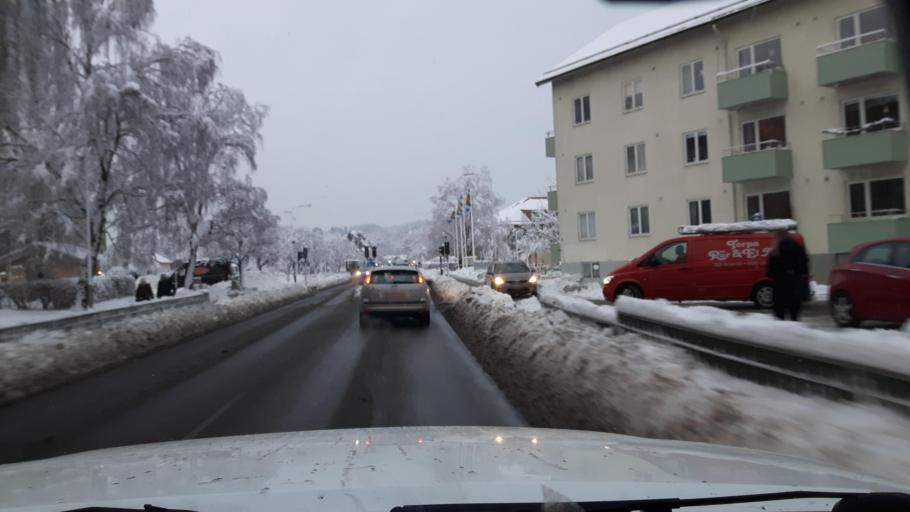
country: SE
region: Vaestra Goetaland
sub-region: Goteborg
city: Goeteborg
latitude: 57.7231
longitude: 11.9347
